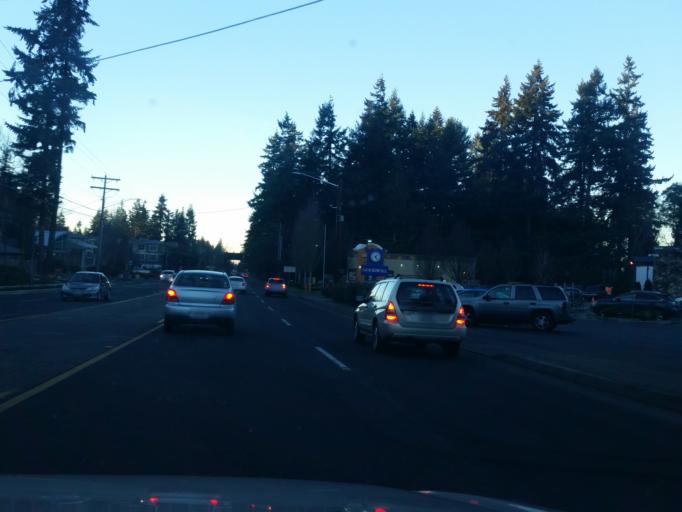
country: US
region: Washington
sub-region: Snohomish County
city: Esperance
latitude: 47.7914
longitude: -122.3687
